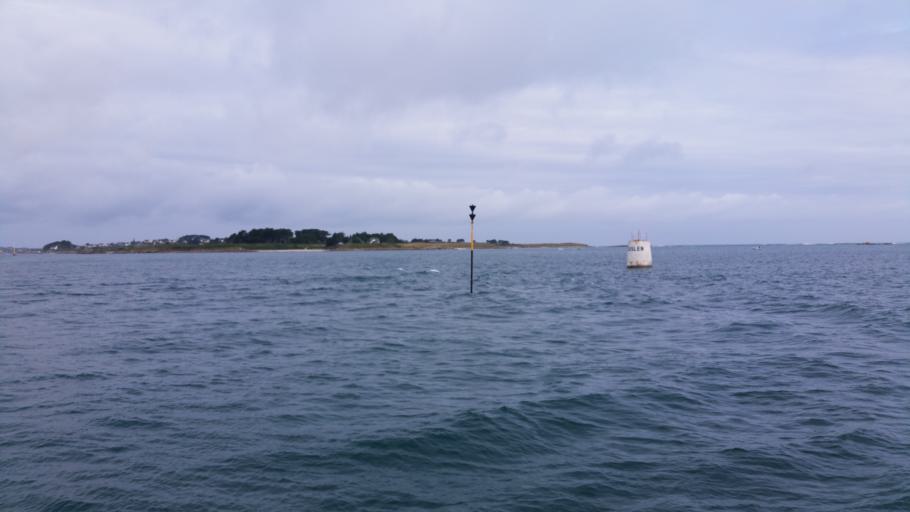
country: FR
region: Brittany
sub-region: Departement du Finistere
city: Roscoff
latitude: 48.7325
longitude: -3.9813
